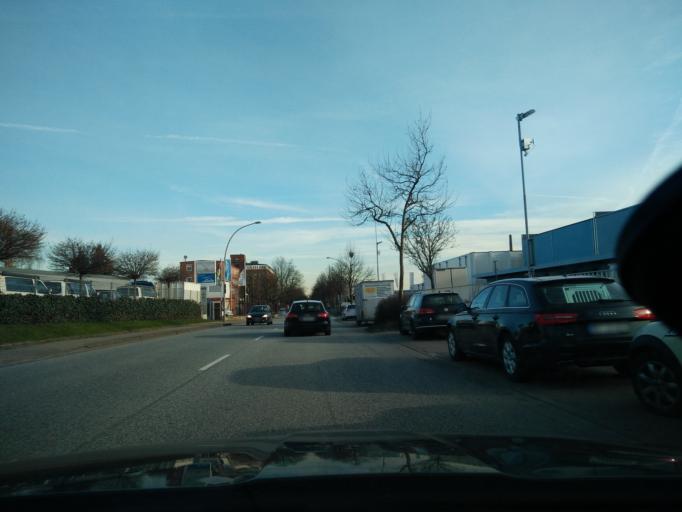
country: DE
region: Hamburg
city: Stellingen
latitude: 53.5767
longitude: 9.9225
